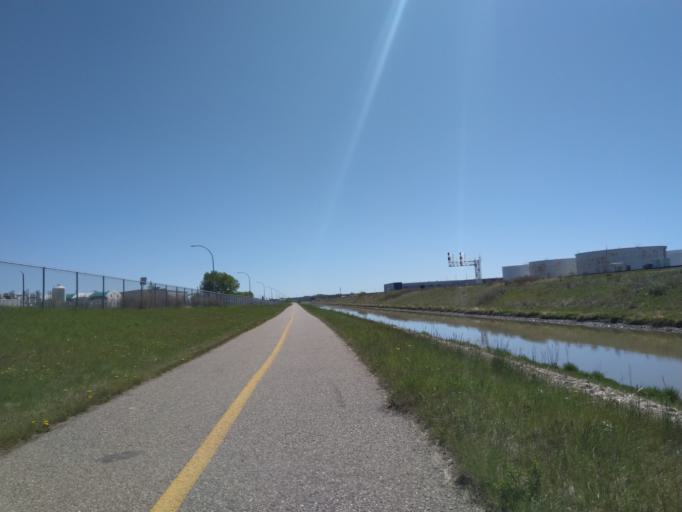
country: CA
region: Alberta
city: Calgary
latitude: 50.9657
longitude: -113.9799
